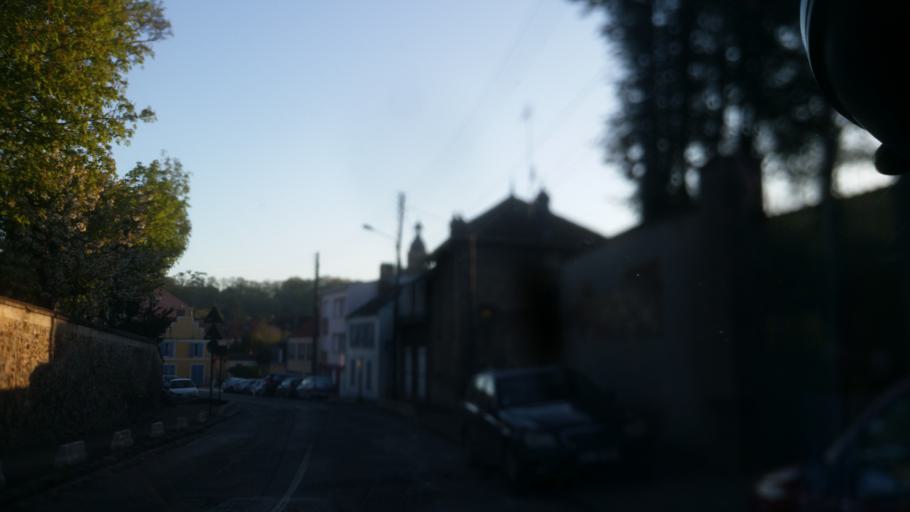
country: FR
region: Ile-de-France
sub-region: Departement de l'Essonne
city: Limours
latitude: 48.6444
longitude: 2.0759
